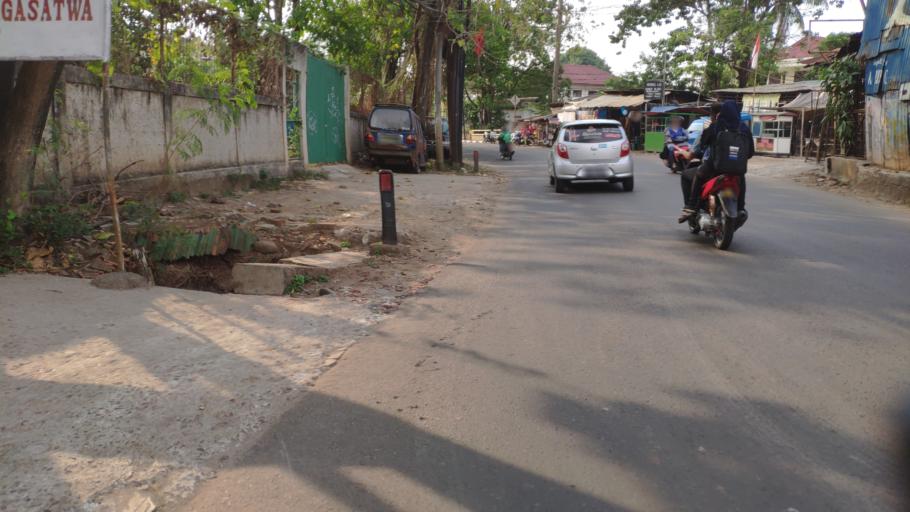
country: ID
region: West Java
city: Pamulang
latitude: -6.3113
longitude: 106.8085
